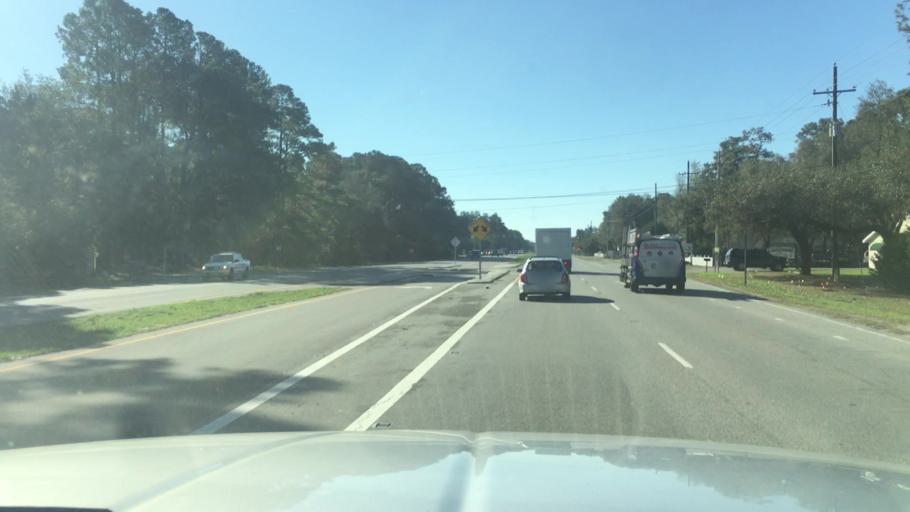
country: US
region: North Carolina
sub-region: New Hanover County
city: Sea Breeze
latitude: 34.0920
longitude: -77.8971
